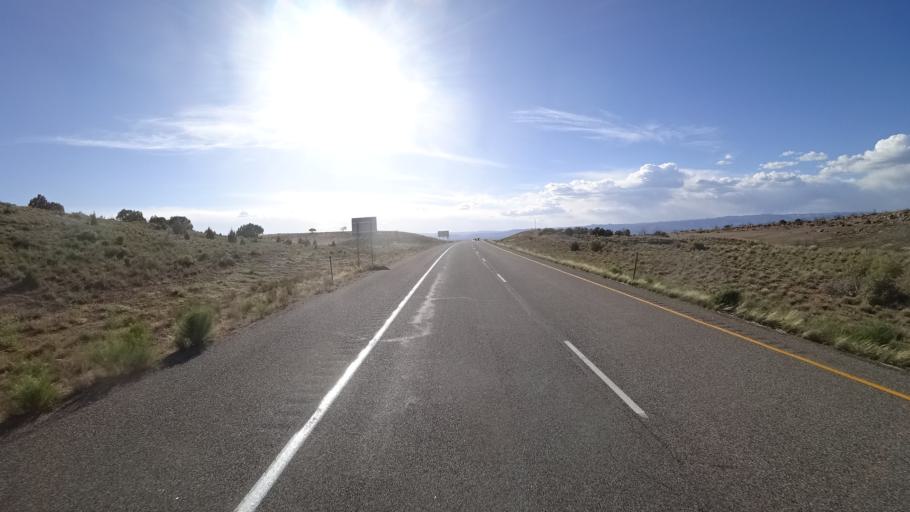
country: US
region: Colorado
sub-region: Mesa County
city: Loma
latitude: 39.1882
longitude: -109.0382
